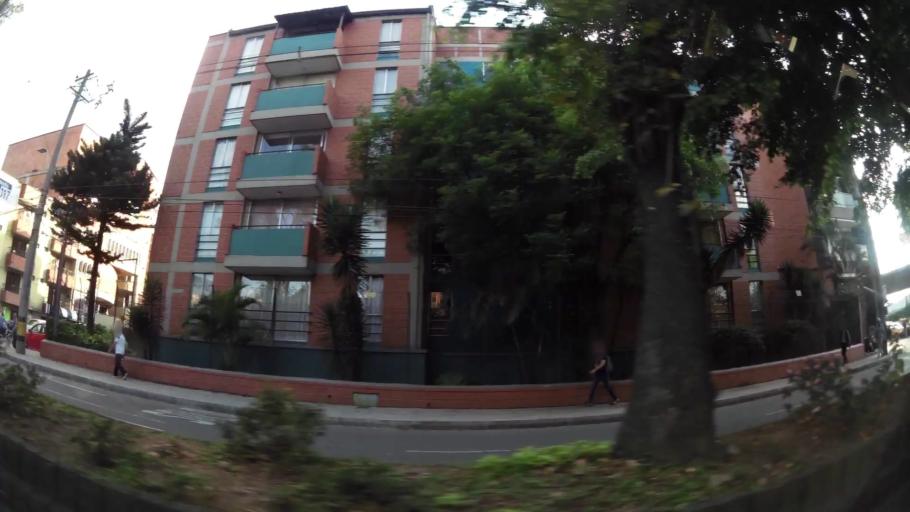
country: CO
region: Antioquia
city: Envigado
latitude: 6.1733
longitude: -75.5919
